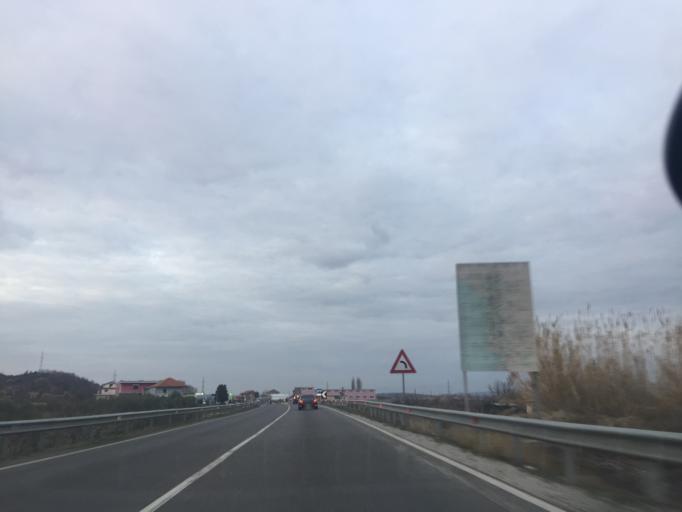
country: AL
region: Shkoder
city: Vukatane
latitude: 41.9769
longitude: 19.5461
